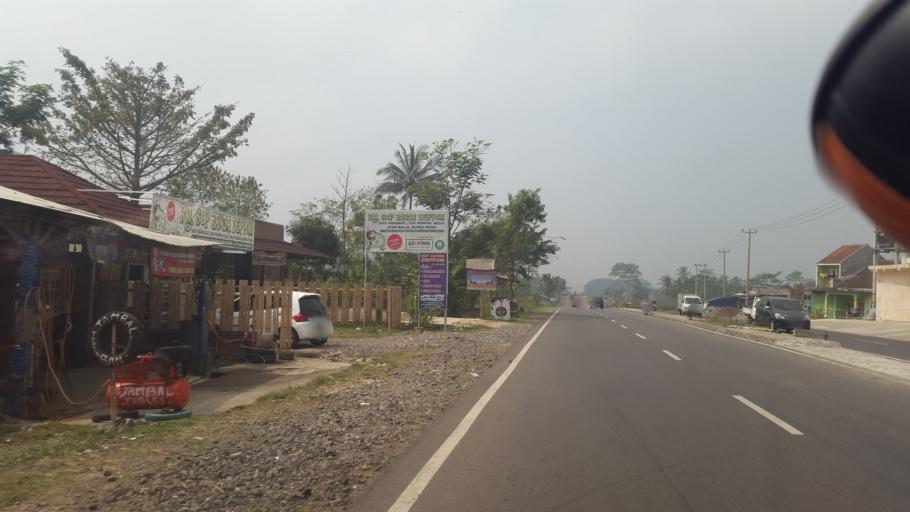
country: ID
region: West Java
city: Sukabumi
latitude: -6.9259
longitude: 106.8956
